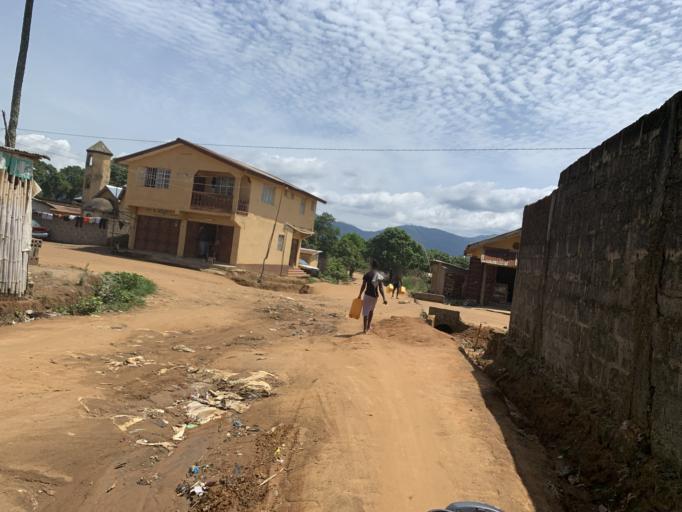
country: SL
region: Western Area
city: Waterloo
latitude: 8.3386
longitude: -13.0526
